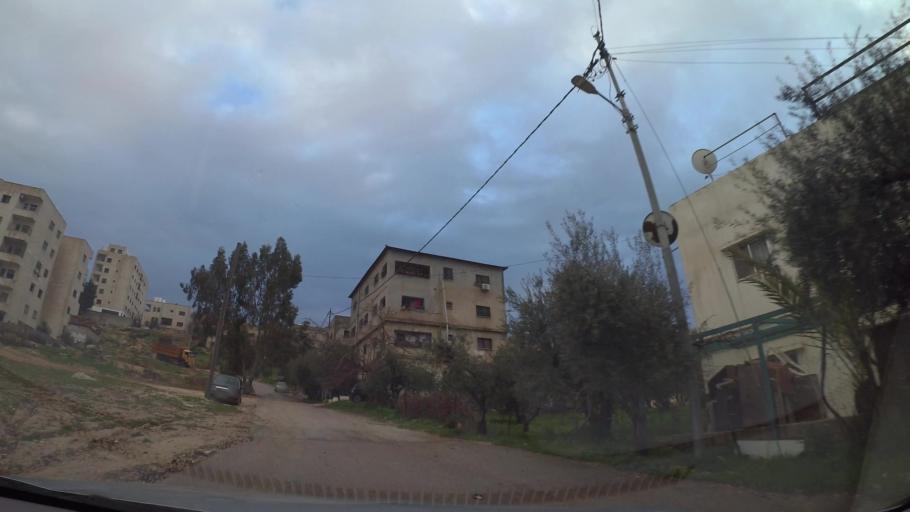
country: JO
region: Amman
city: Al Jubayhah
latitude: 32.0333
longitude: 35.8284
